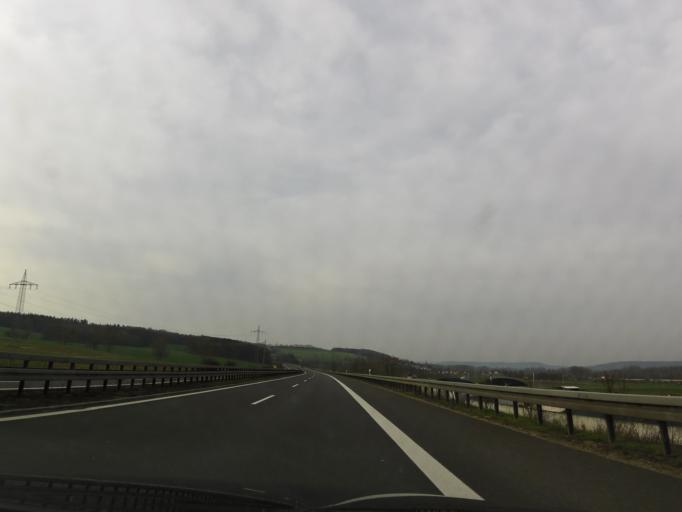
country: DE
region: Bavaria
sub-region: Upper Franconia
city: Ebensfeld
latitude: 50.0531
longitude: 10.9618
